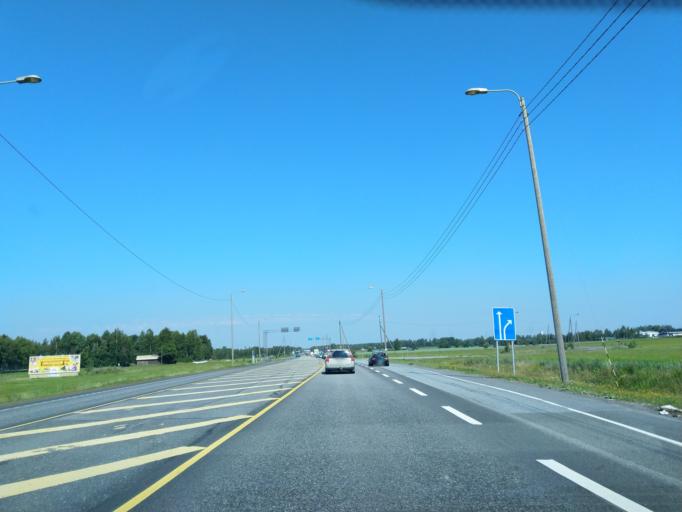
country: FI
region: Satakunta
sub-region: Pori
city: Nakkila
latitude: 61.3492
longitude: 22.0158
